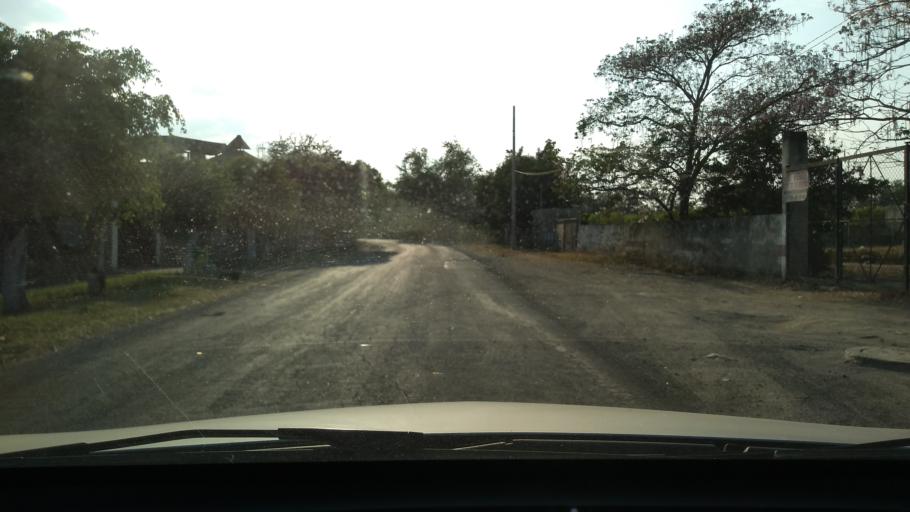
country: MX
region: Morelos
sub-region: Jojutla
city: Tehuixtla
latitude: 18.5636
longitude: -99.2703
